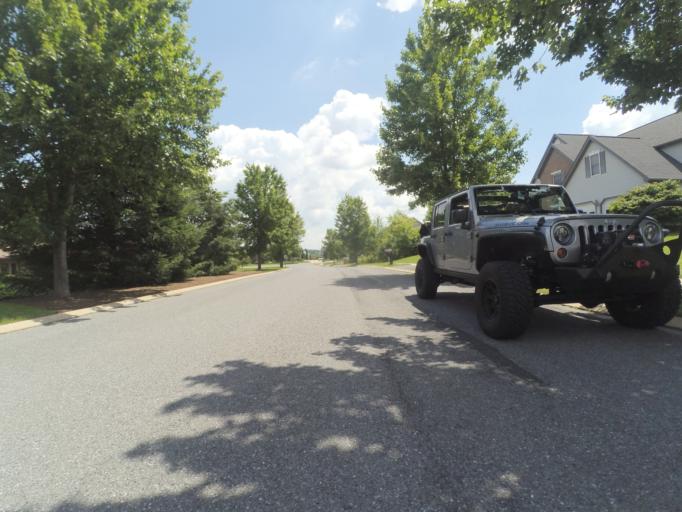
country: US
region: Pennsylvania
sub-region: Centre County
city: State College
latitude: 40.7775
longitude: -77.8460
